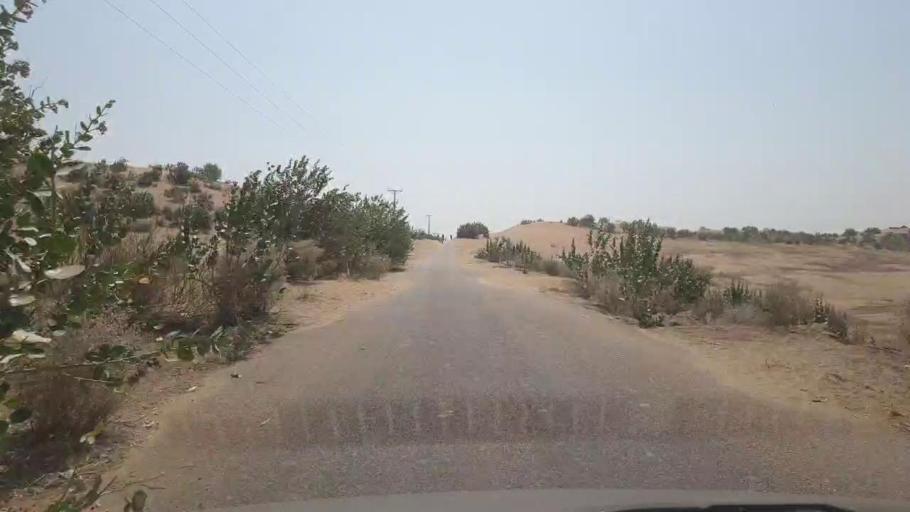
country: PK
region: Sindh
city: Chor
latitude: 25.6180
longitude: 70.1763
